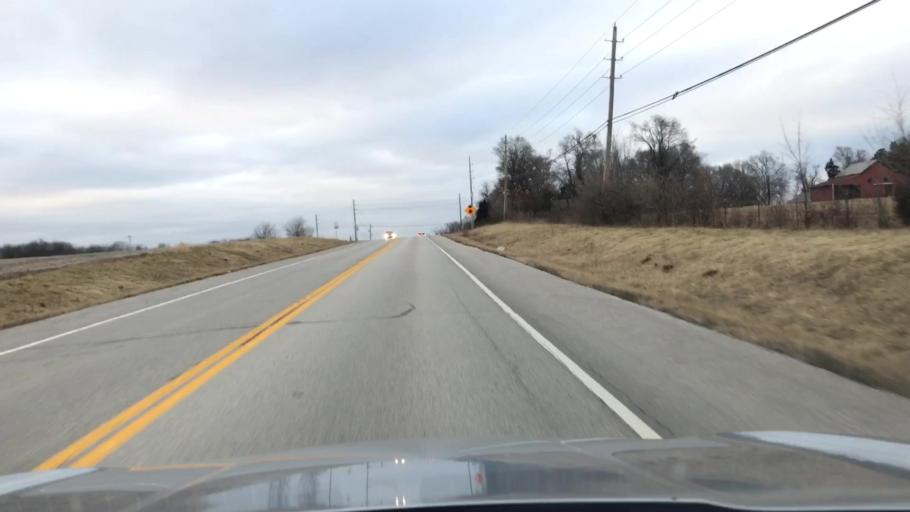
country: US
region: Missouri
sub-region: Jackson County
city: Lees Summit
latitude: 38.8879
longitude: -94.4151
